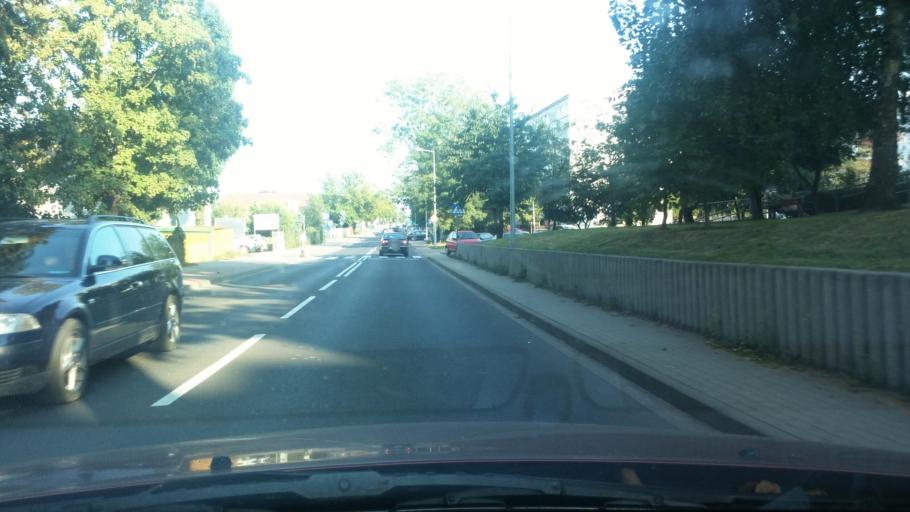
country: PL
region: Lower Silesian Voivodeship
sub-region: Powiat zgorzelecki
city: Zgorzelec
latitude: 51.1594
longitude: 15.0018
